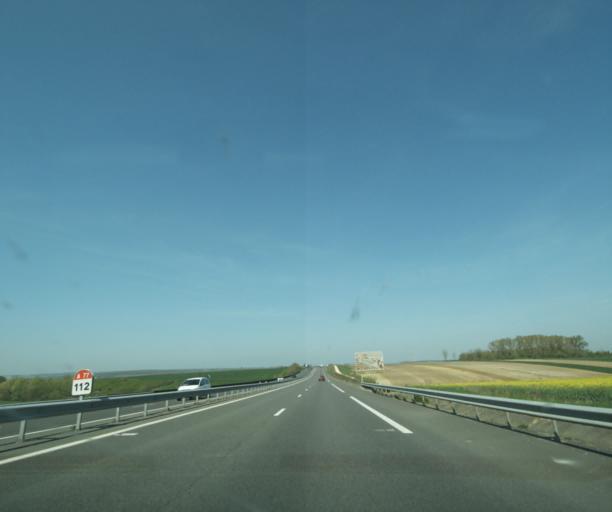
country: FR
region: Bourgogne
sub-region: Departement de la Nievre
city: Pouilly-sur-Loire
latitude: 47.3153
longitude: 2.9400
